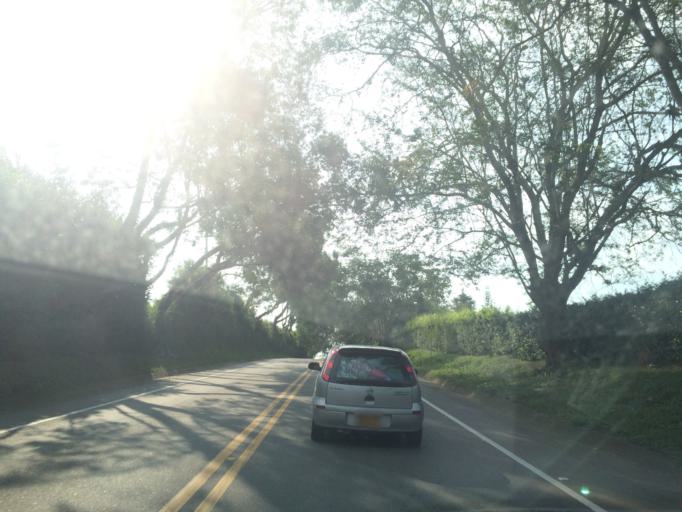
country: CO
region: Quindio
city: La Tebaida
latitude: 4.4478
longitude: -75.8216
